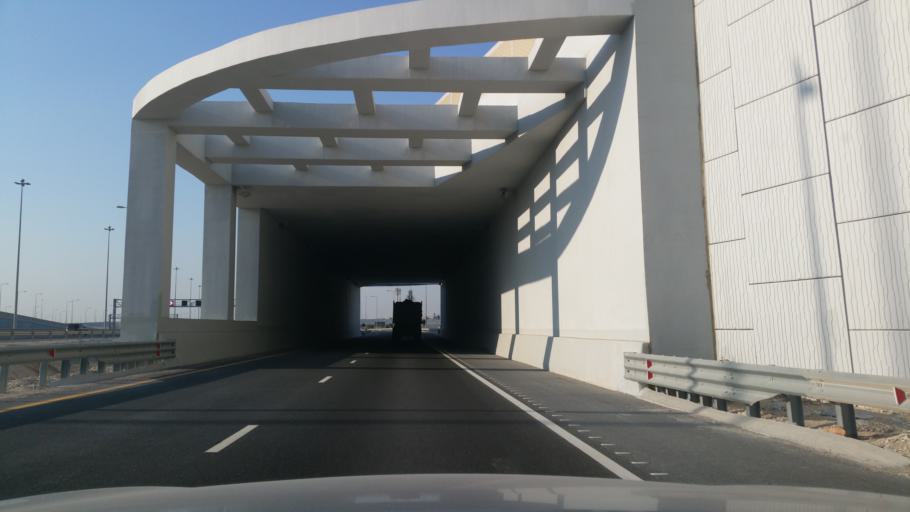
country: QA
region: Al Wakrah
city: Al Wakrah
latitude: 25.1557
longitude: 51.5726
